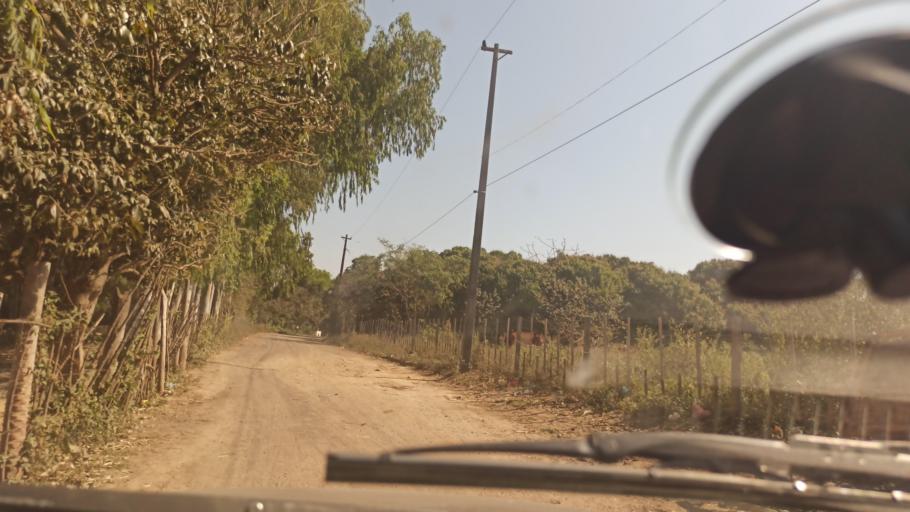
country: AR
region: Formosa
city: Clorinda
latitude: -25.3032
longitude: -57.7008
